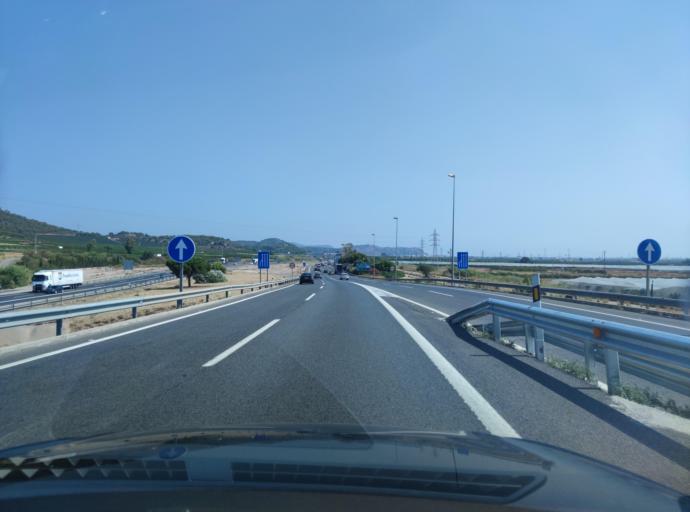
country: ES
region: Valencia
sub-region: Provincia de Valencia
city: Pucol
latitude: 39.6347
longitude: -0.3034
